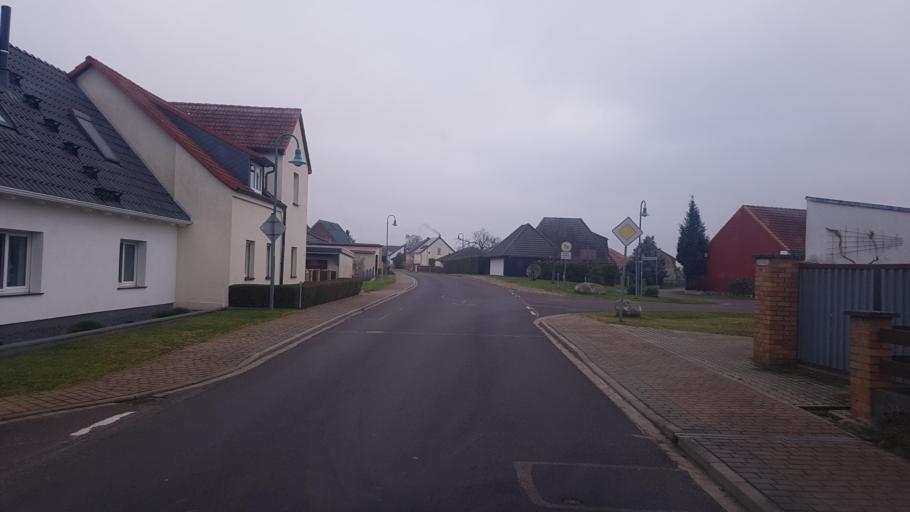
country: DE
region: Brandenburg
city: Gross Kreutz
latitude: 52.3799
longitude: 12.7942
